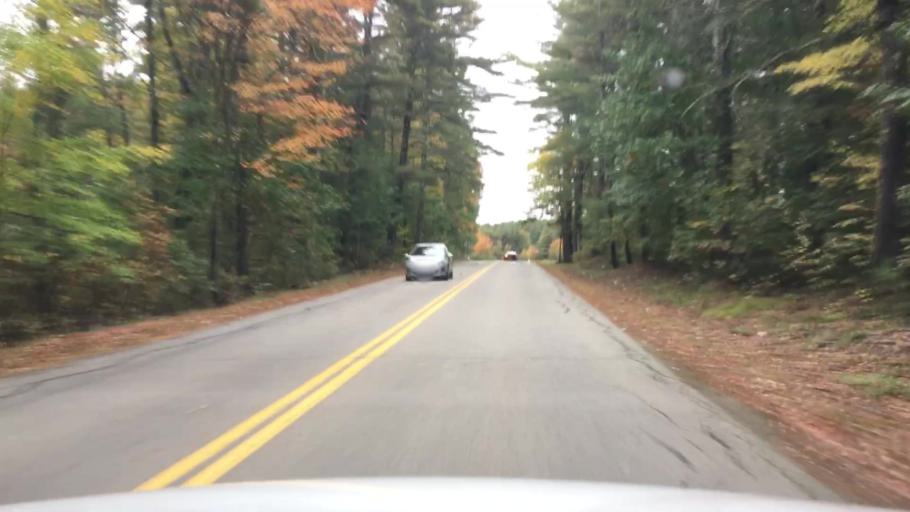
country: US
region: Maine
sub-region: York County
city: Berwick
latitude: 43.2841
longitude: -70.9039
